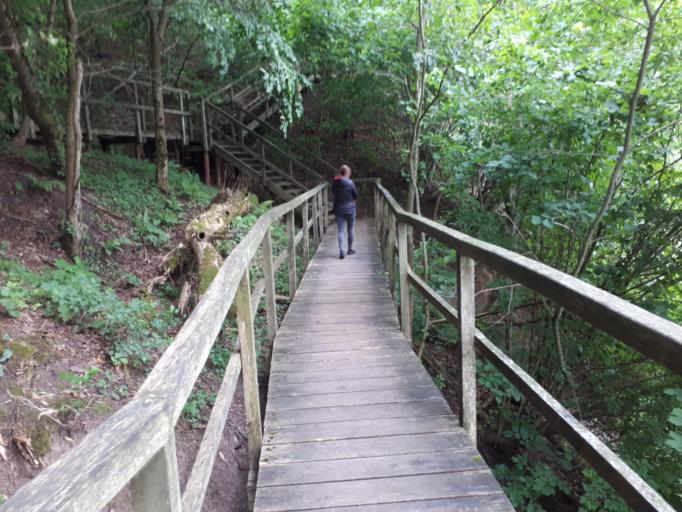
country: LT
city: Ramuciai
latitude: 54.8884
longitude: 24.0741
